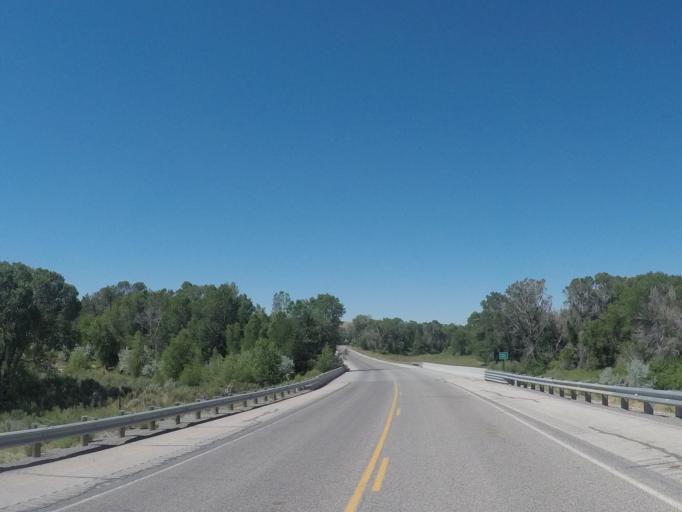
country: US
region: Wyoming
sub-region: Big Horn County
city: Greybull
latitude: 44.5441
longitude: -107.7736
